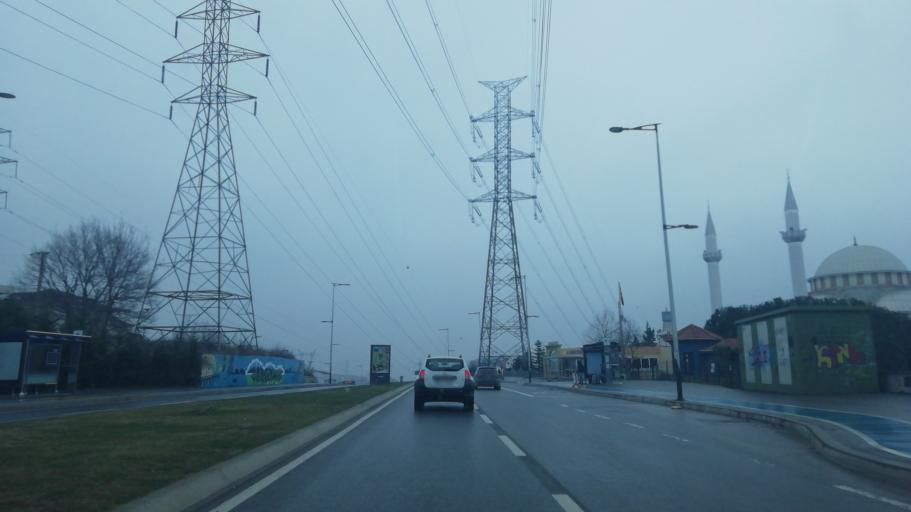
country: TR
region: Sakarya
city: Adapazari
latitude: 40.7458
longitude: 30.3459
